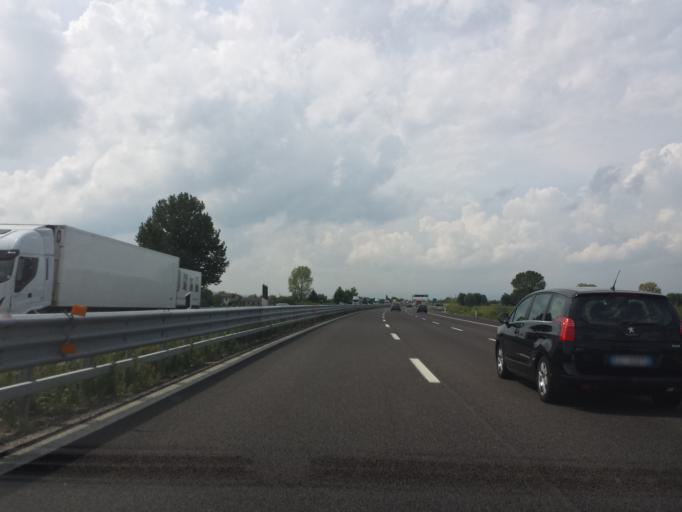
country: IT
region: Veneto
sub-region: Provincia di Padova
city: Arlesega
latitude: 45.4692
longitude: 11.7355
